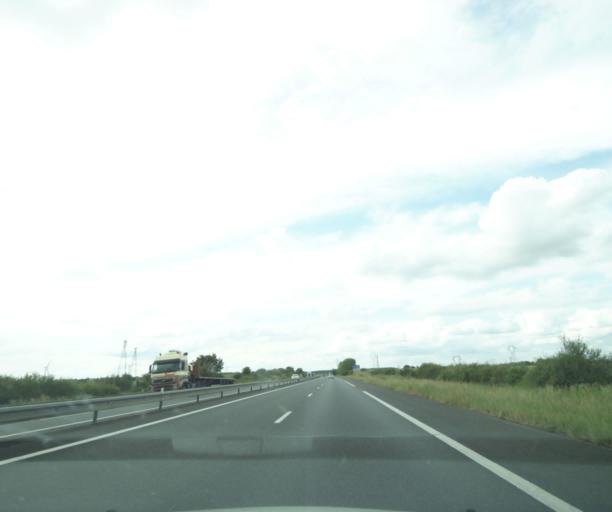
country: FR
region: Centre
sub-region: Departement du Cher
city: Marmagne
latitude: 47.0858
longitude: 2.2610
